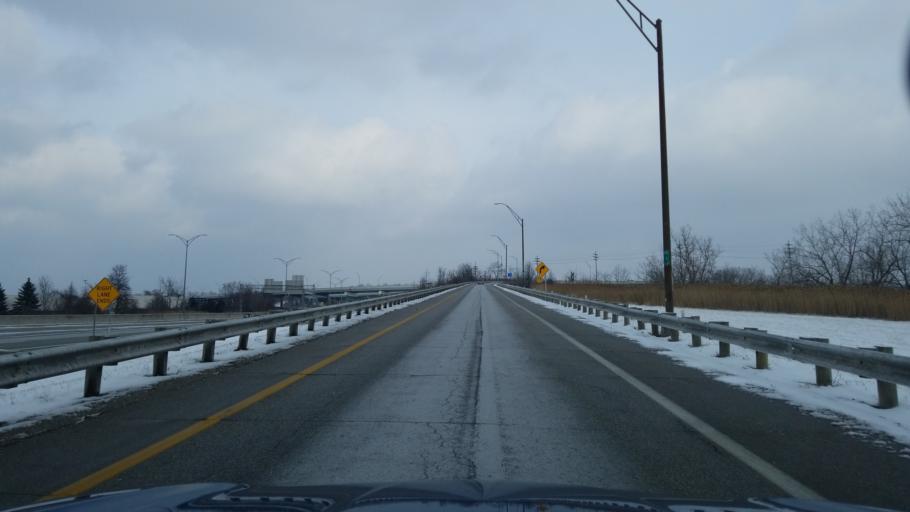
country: US
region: Ohio
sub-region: Cuyahoga County
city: Brook Park
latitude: 41.4222
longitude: -81.8251
